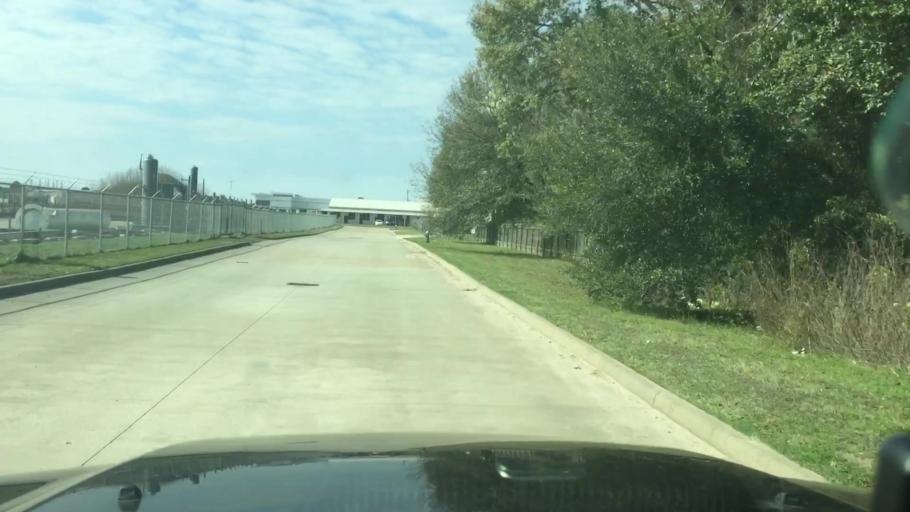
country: US
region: Texas
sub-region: Harris County
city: Hudson
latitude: 29.9204
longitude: -95.5266
